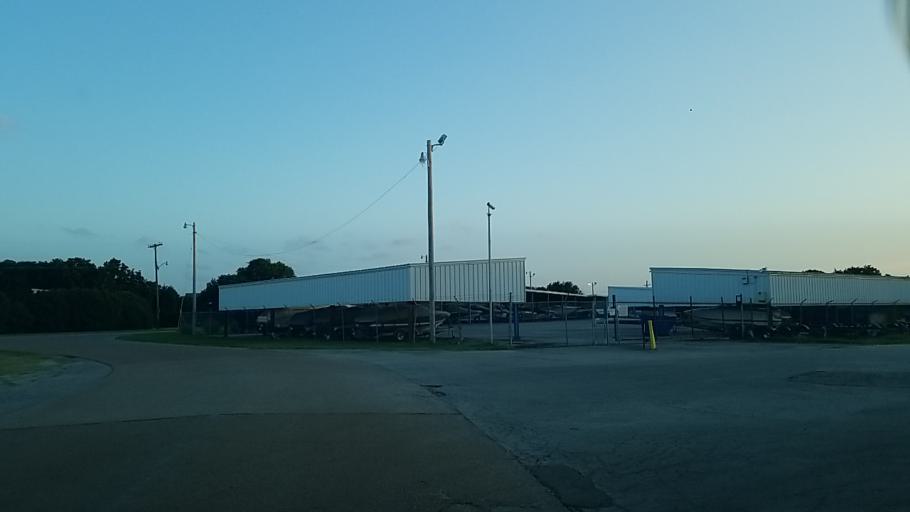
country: US
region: Texas
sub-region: Denton County
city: Highland Village
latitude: 33.0828
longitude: -97.0222
